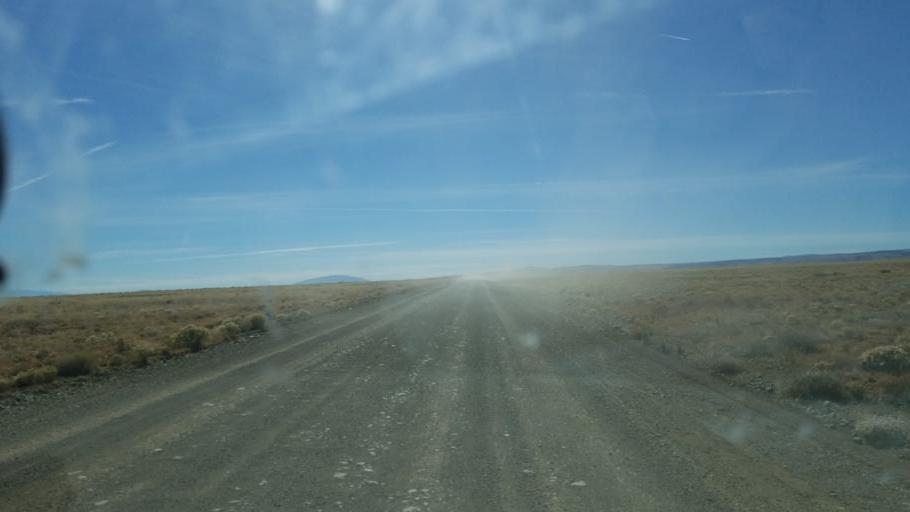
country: US
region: Colorado
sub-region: Rio Grande County
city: Monte Vista
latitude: 37.3470
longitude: -106.1491
